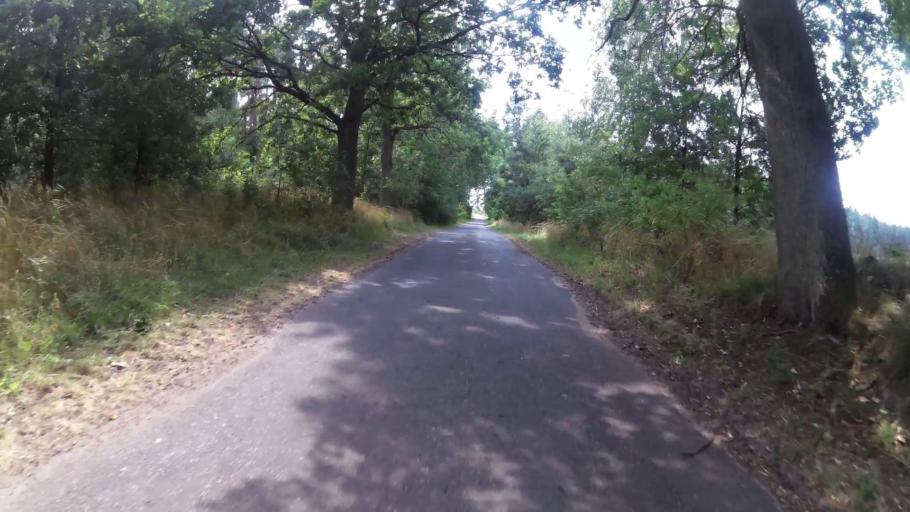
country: PL
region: West Pomeranian Voivodeship
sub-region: Powiat gryfinski
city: Mieszkowice
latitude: 52.8729
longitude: 14.5241
